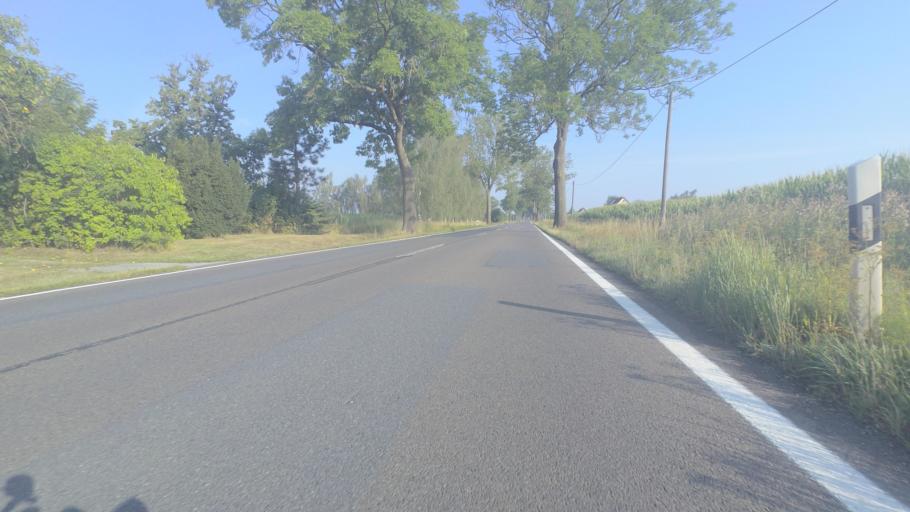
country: DE
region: Mecklenburg-Vorpommern
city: Grimmen
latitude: 54.0448
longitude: 13.1218
